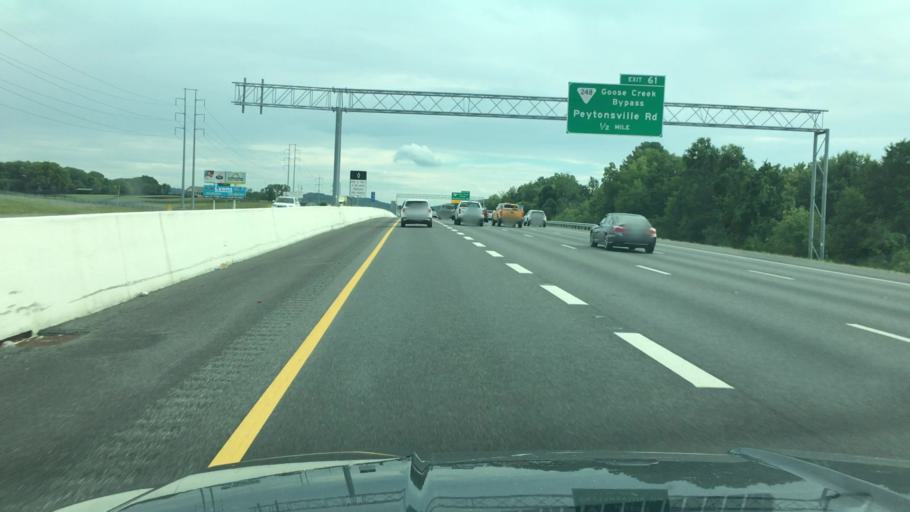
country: US
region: Tennessee
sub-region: Williamson County
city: Franklin
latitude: 35.8740
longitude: -86.8310
